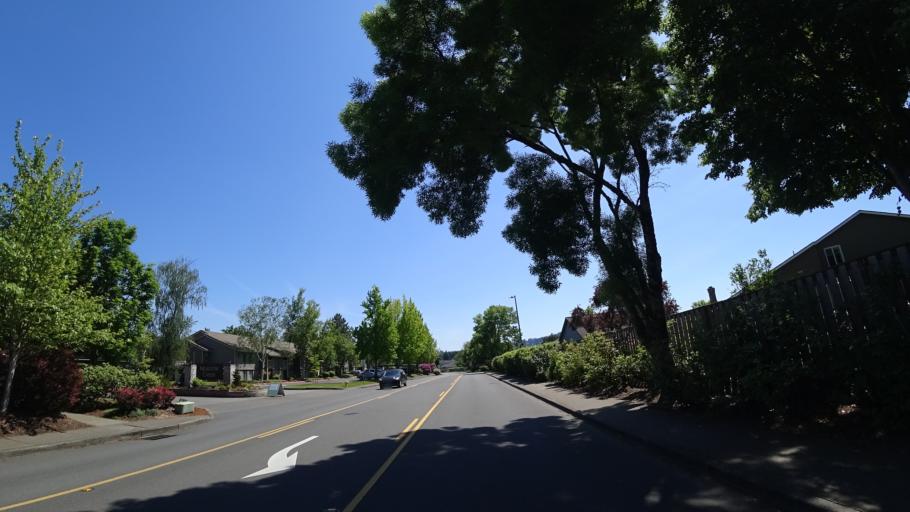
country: US
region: Oregon
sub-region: Washington County
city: Tigard
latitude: 45.4424
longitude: -122.8055
